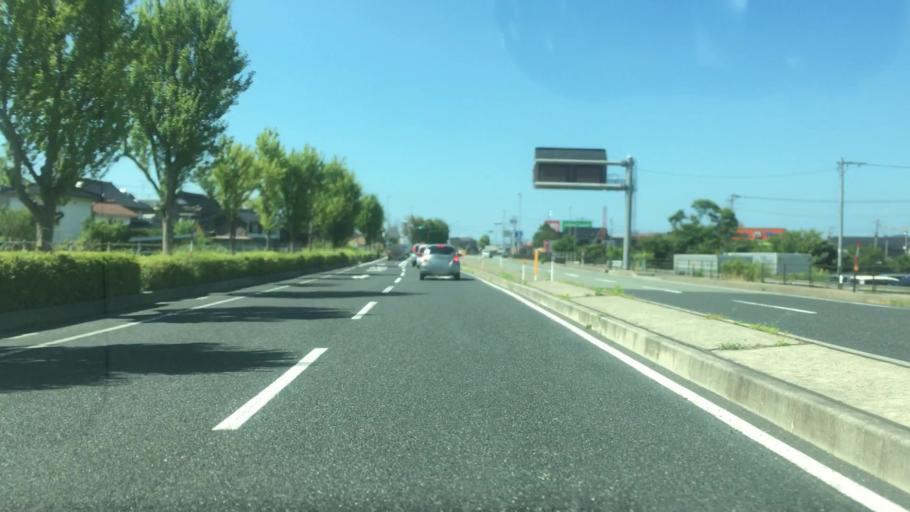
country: JP
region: Tottori
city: Tottori
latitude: 35.4726
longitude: 134.2172
